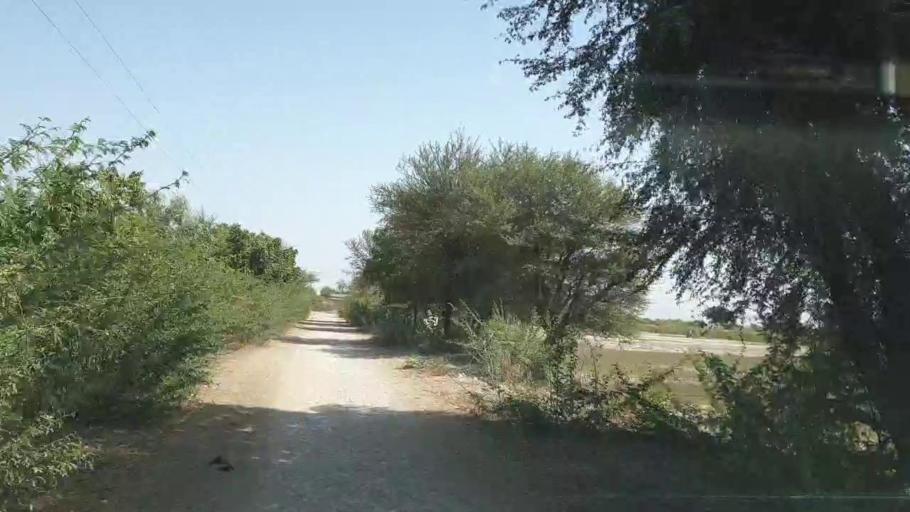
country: PK
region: Sindh
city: Naukot
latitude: 24.9570
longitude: 69.4889
